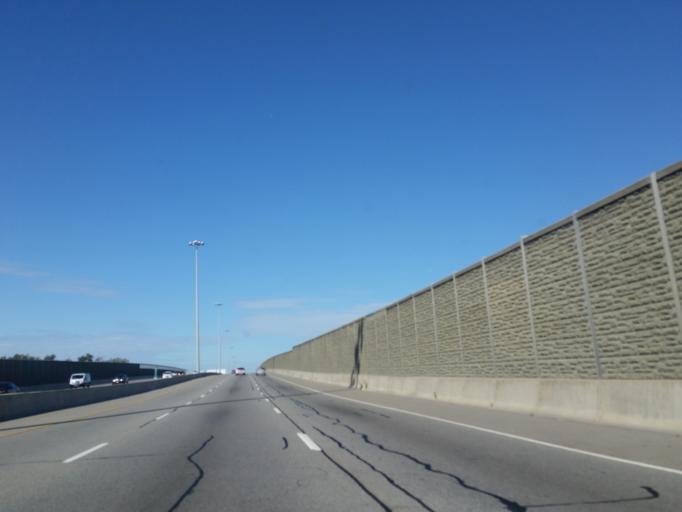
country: CA
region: Ontario
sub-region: Regional Municipality of Niagara
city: St. Catharines
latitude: 43.1705
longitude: -79.2193
